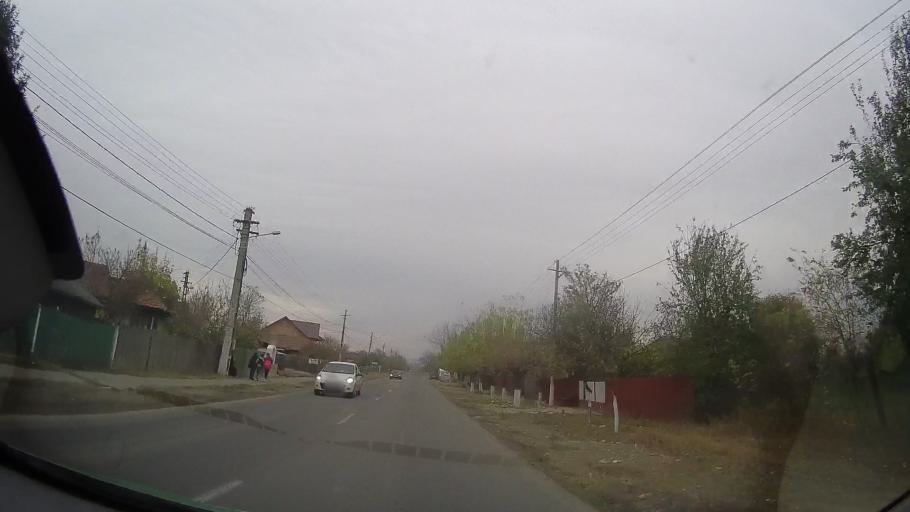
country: RO
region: Prahova
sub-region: Comuna Albesti-Paleologu
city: Albesti-Paleologu
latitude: 44.9567
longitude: 26.2309
